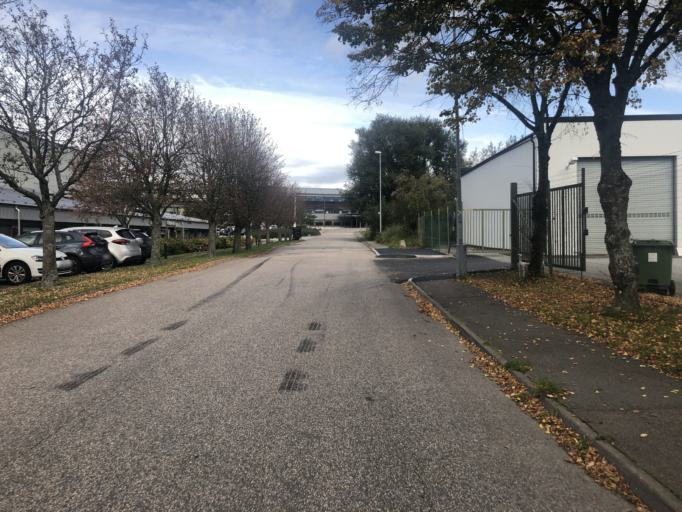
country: SE
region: Vaestra Goetaland
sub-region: Molndal
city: Moelndal
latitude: 57.6487
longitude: 11.9913
